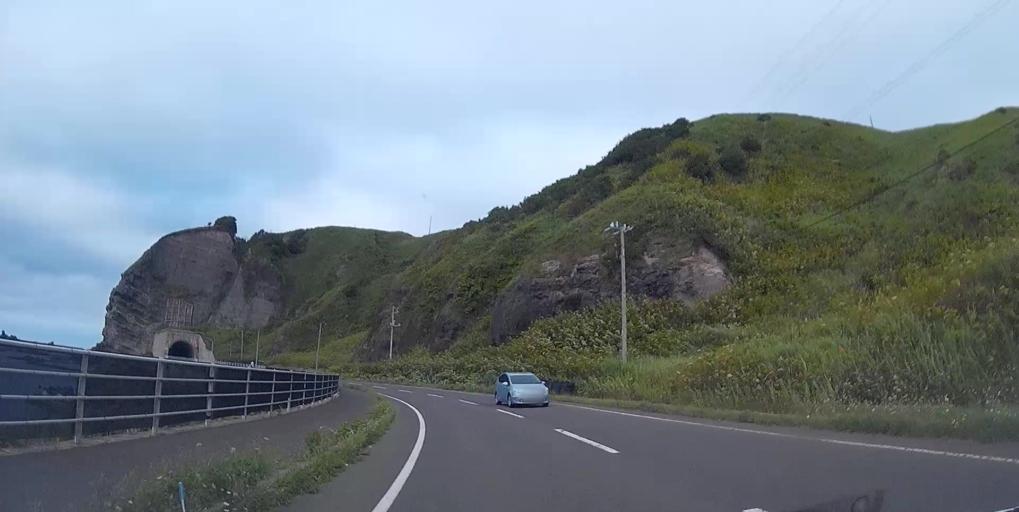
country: JP
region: Hokkaido
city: Iwanai
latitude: 42.3844
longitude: 139.8189
